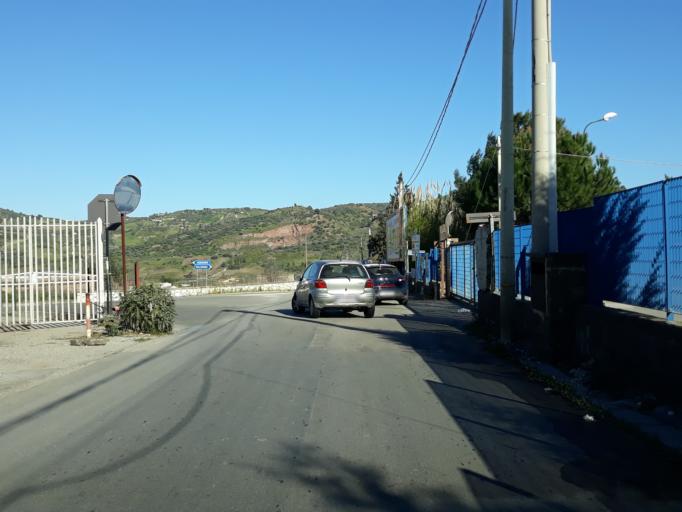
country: IT
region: Sicily
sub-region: Palermo
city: Misilmeri
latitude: 38.0276
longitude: 13.4543
